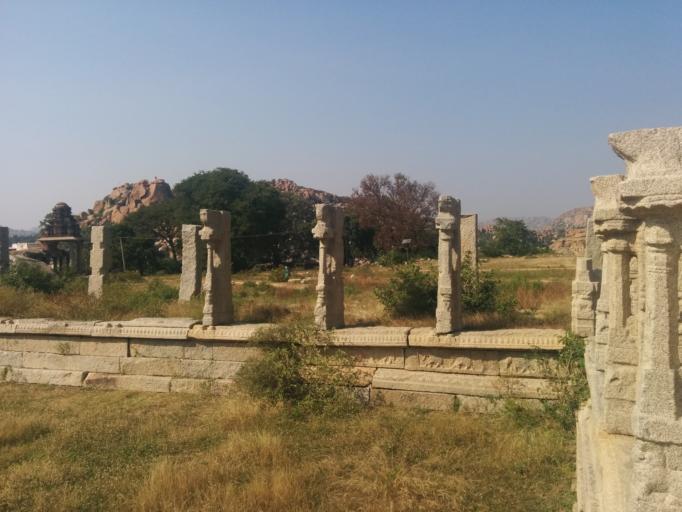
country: IN
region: Karnataka
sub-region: Bellary
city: Hampi
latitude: 15.3352
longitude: 76.4696
